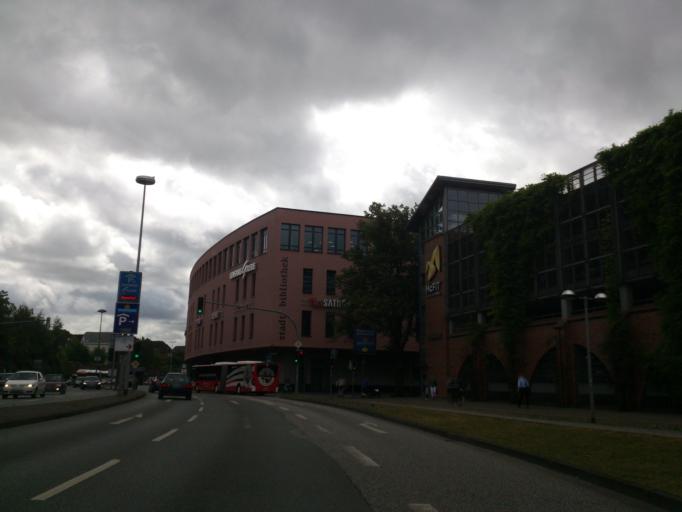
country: DE
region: Schleswig-Holstein
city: Flensburg
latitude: 54.7846
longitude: 9.4382
